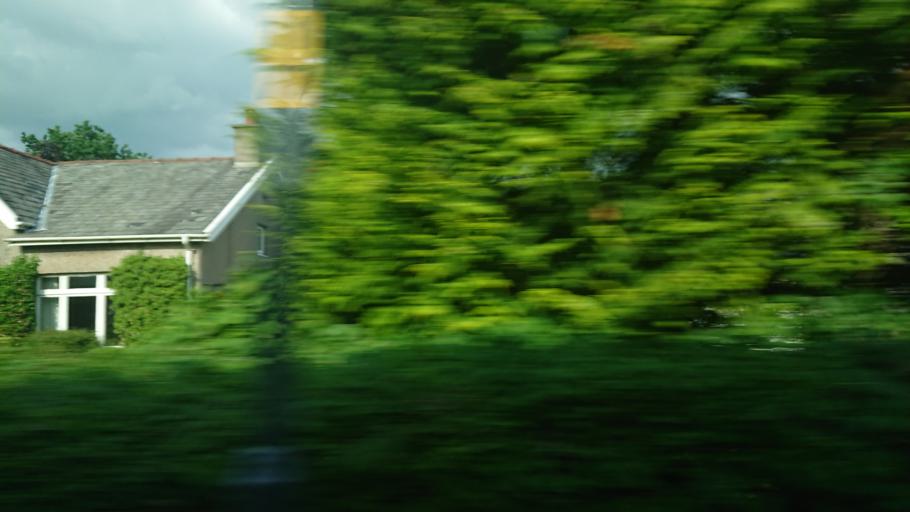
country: GB
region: England
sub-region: North Yorkshire
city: High Bentham
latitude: 54.1226
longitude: -2.5076
